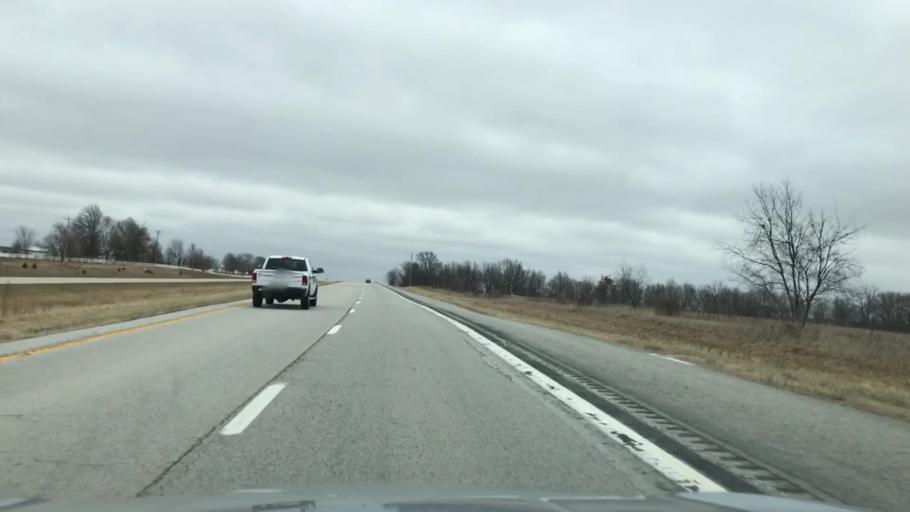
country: US
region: Missouri
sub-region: Linn County
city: Linneus
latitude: 39.7772
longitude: -93.3529
